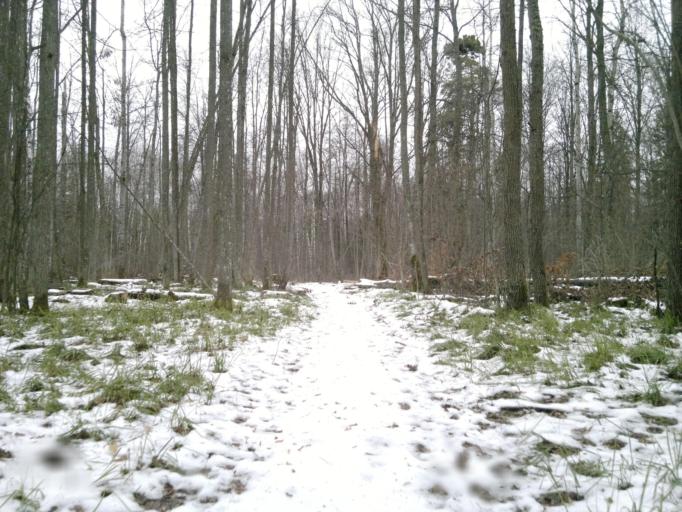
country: RU
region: Mariy-El
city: Yoshkar-Ola
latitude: 56.6130
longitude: 47.9460
